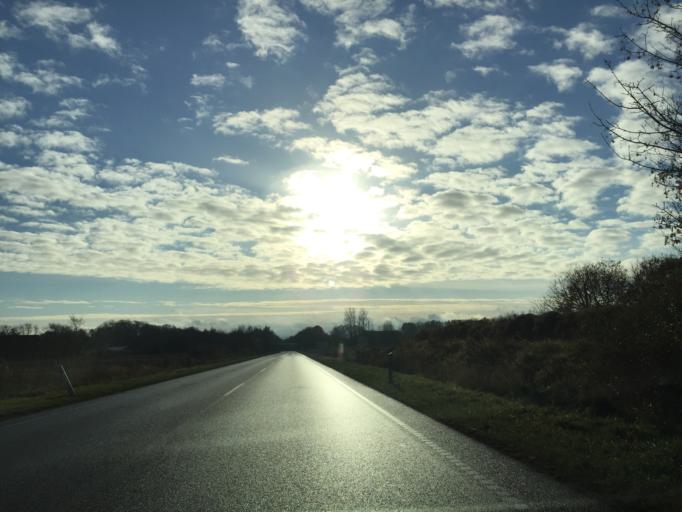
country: DK
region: Central Jutland
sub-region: Arhus Kommune
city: Framlev
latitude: 56.1897
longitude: 10.0067
